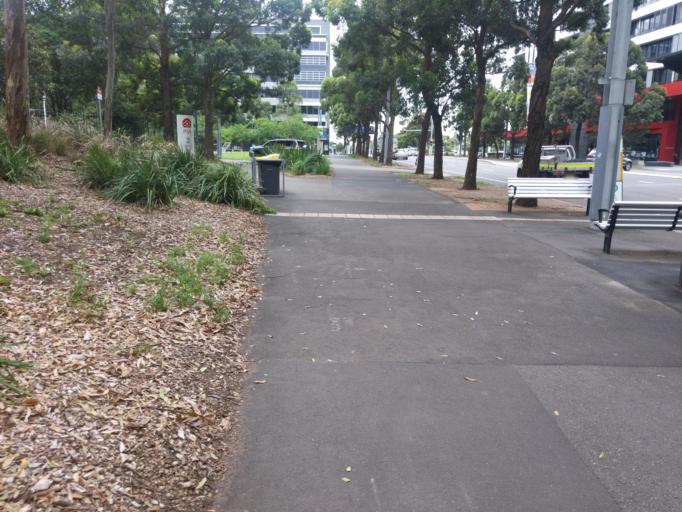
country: AU
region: New South Wales
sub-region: Canada Bay
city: Concord West
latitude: -33.8476
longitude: 151.0727
